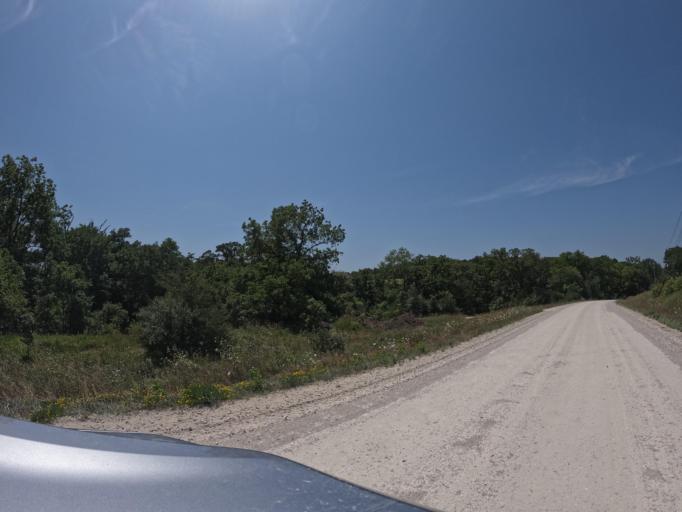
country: US
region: Iowa
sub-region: Henry County
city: Mount Pleasant
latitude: 40.9268
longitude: -91.6286
